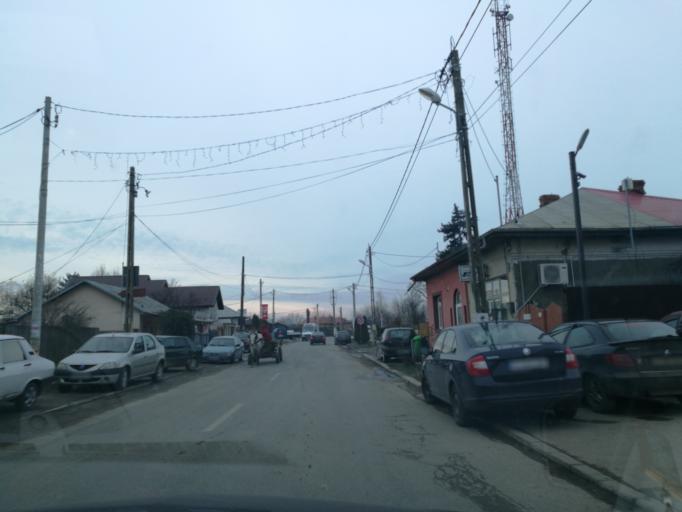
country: RO
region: Ialomita
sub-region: Comuna Fierbinti-Targ
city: Fierbintii de Jos
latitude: 44.6824
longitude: 26.3831
